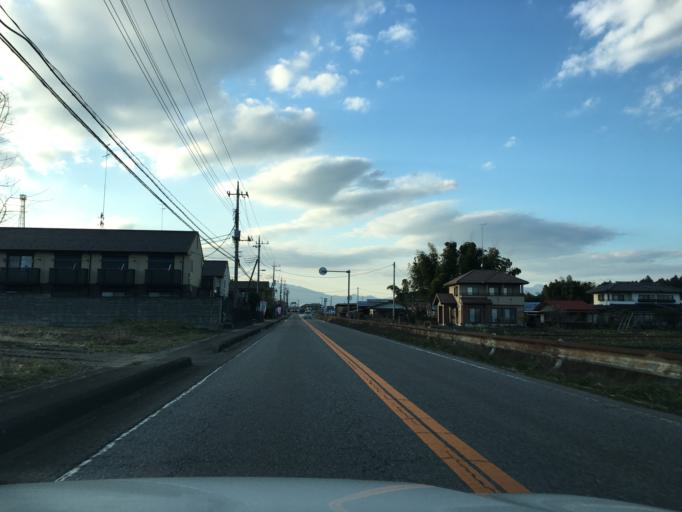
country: JP
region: Tochigi
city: Otawara
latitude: 36.8702
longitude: 140.0763
